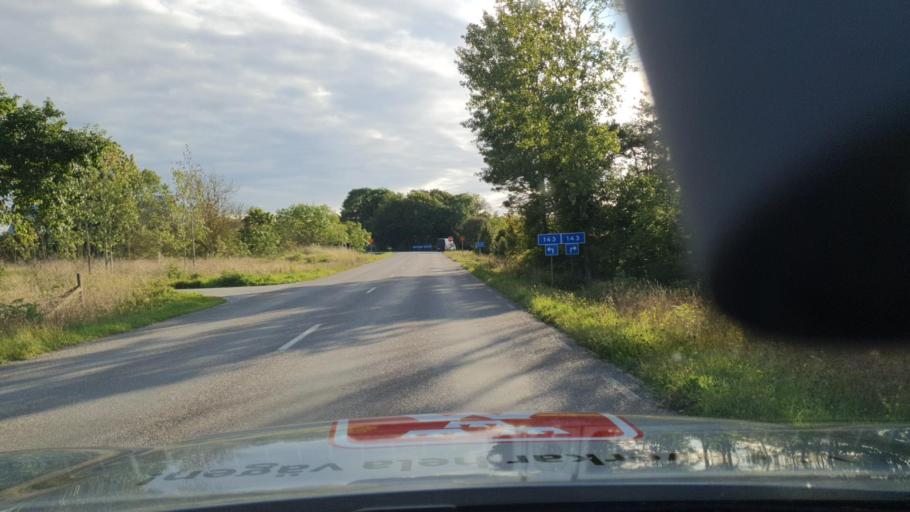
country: SE
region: Gotland
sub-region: Gotland
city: Hemse
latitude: 57.4299
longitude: 18.6325
